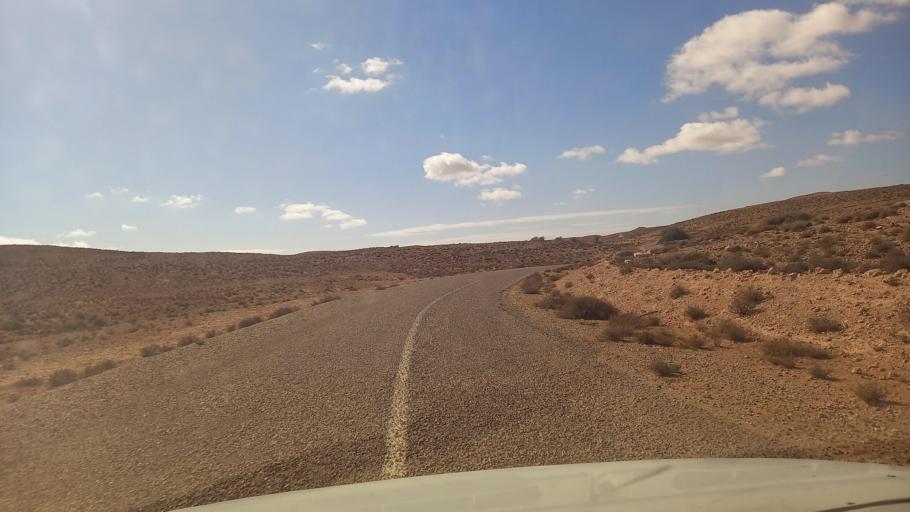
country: TN
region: Tataouine
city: Tataouine
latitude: 32.8778
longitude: 10.2400
